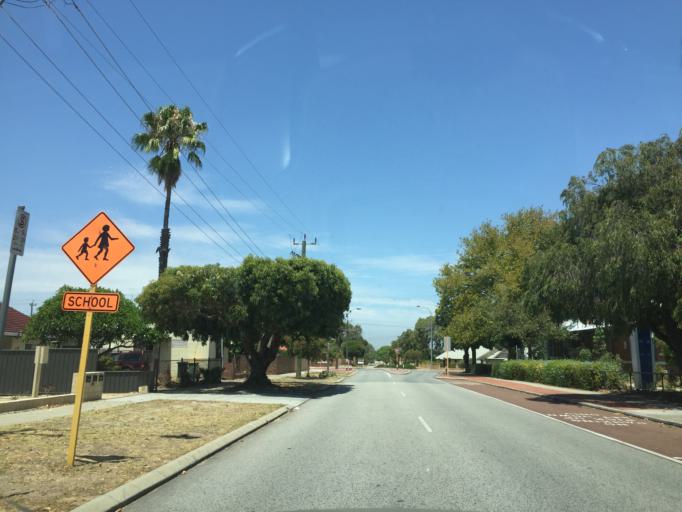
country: AU
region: Western Australia
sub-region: Canning
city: Queens Park
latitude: -31.9994
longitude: 115.9445
